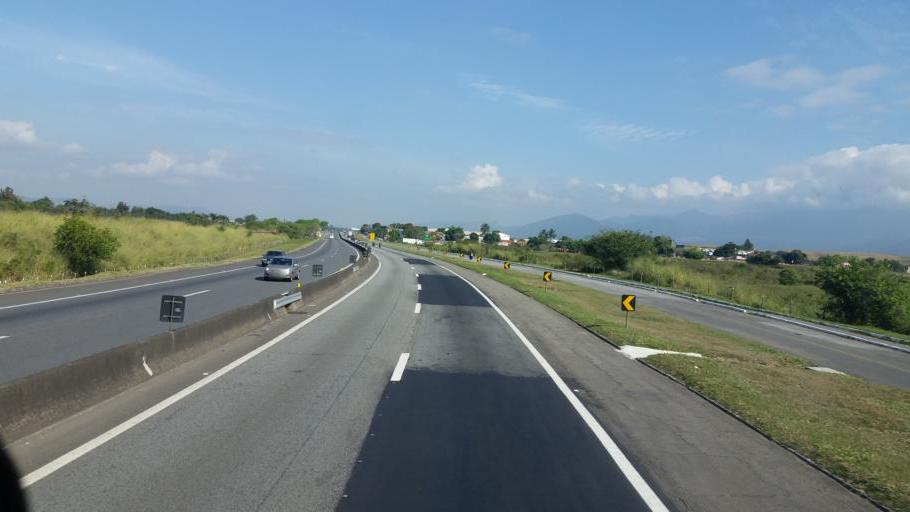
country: BR
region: Rio de Janeiro
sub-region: Resende
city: Resende
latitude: -22.4603
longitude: -44.4721
